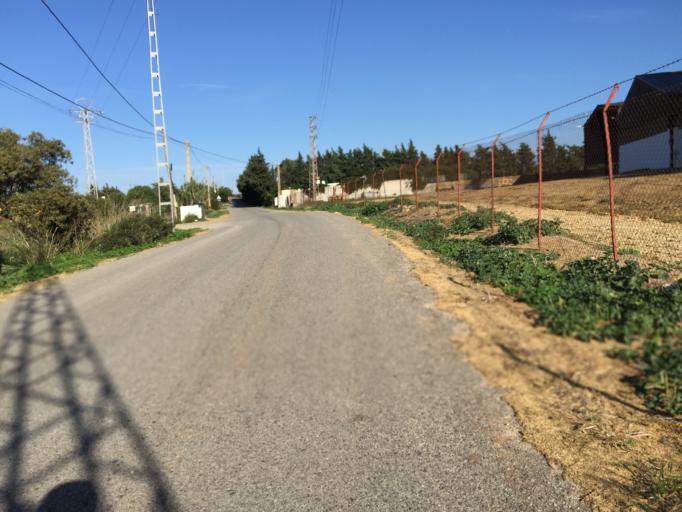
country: ES
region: Andalusia
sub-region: Provincia de Cadiz
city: Vejer de la Frontera
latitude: 36.2695
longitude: -6.0046
